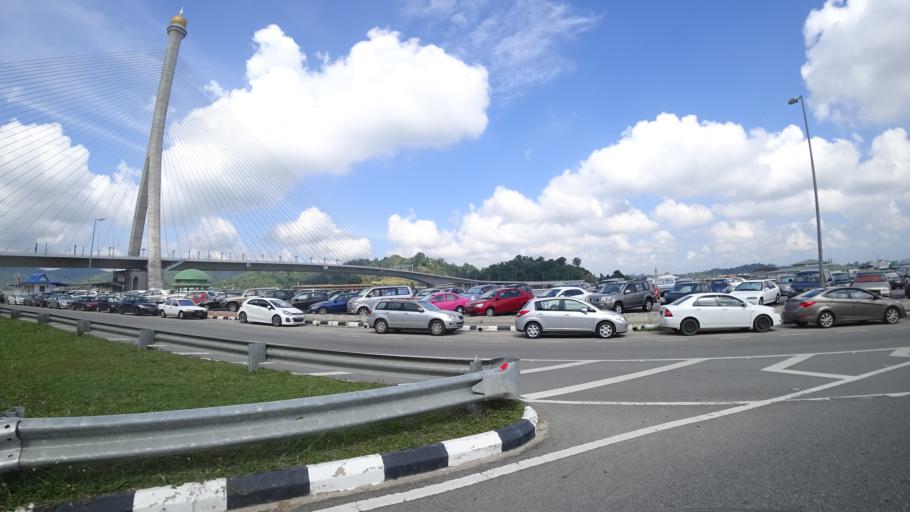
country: BN
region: Brunei and Muara
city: Bandar Seri Begawan
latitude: 4.8782
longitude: 114.9508
